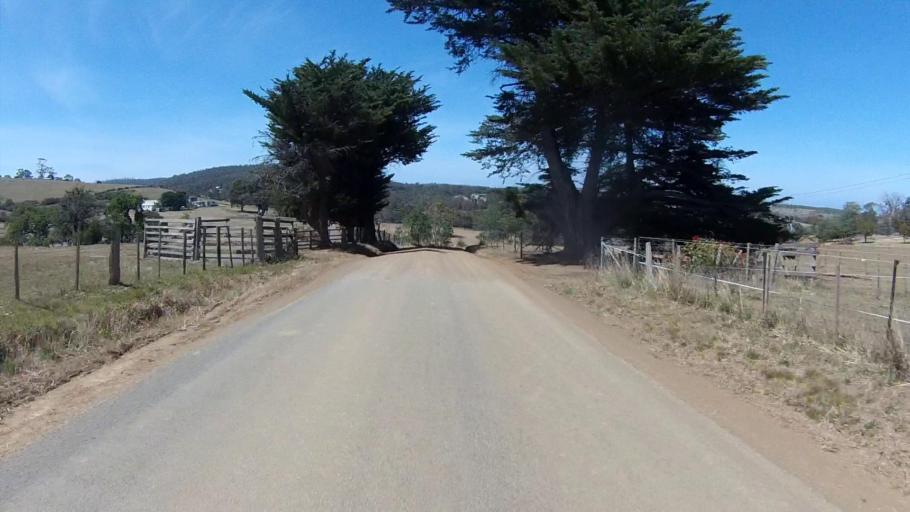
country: AU
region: Tasmania
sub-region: Sorell
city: Sorell
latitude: -42.7949
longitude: 147.6402
